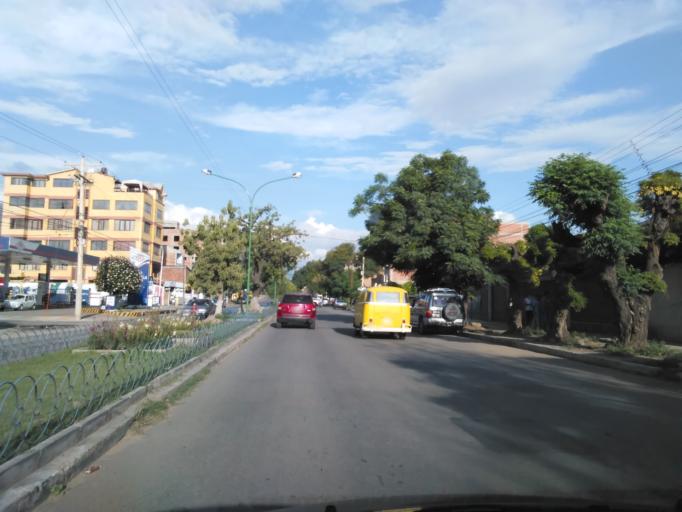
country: BO
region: Cochabamba
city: Cochabamba
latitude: -17.3657
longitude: -66.1738
